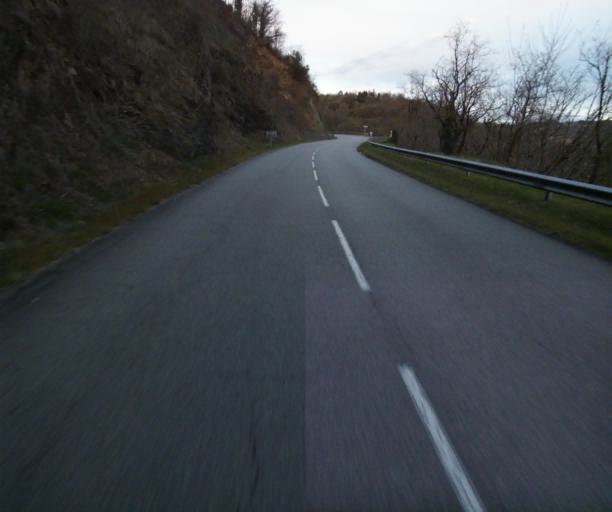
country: FR
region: Limousin
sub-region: Departement de la Correze
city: Laguenne
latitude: 45.2511
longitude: 1.7908
